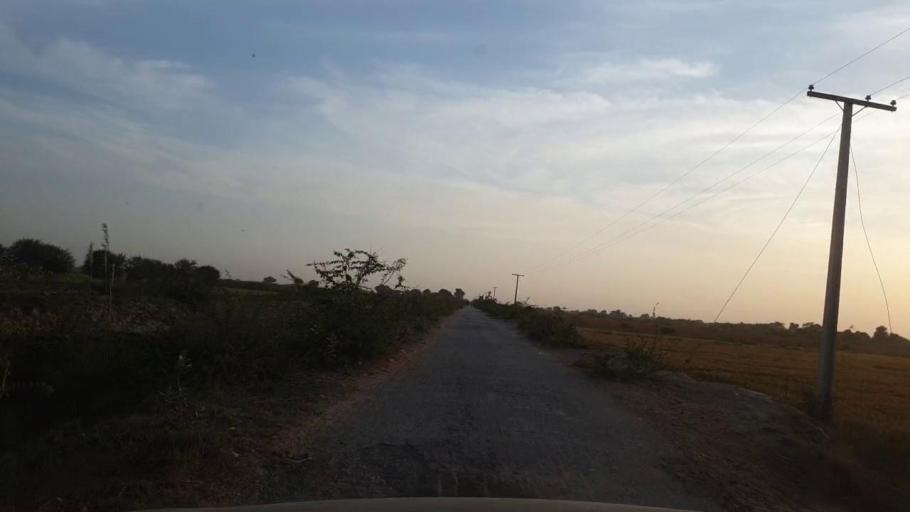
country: PK
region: Sindh
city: Kunri
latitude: 25.1450
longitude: 69.5808
